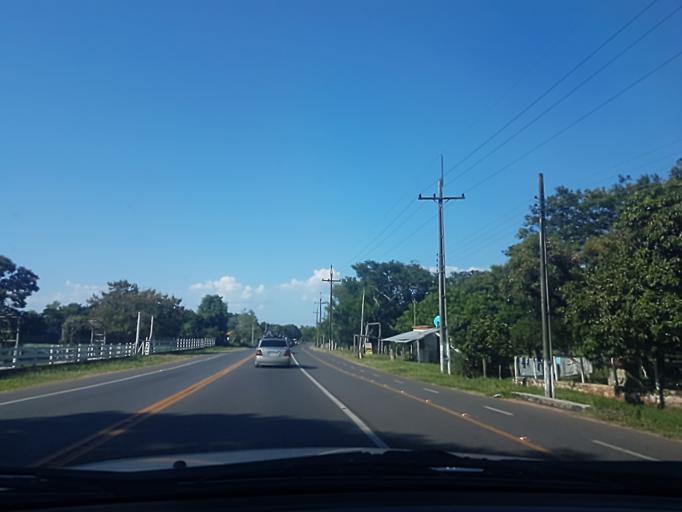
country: PY
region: Central
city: Aregua
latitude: -25.2334
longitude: -57.4202
